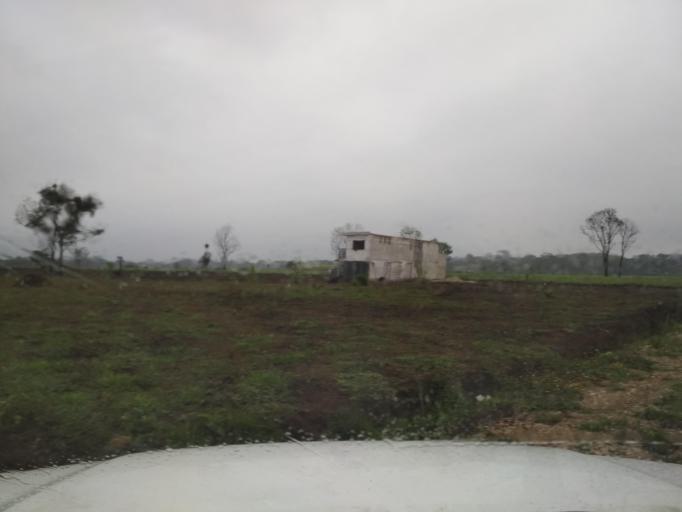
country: MX
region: Veracruz
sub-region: Cordoba
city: Veinte de Noviembre
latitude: 18.8594
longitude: -96.9601
